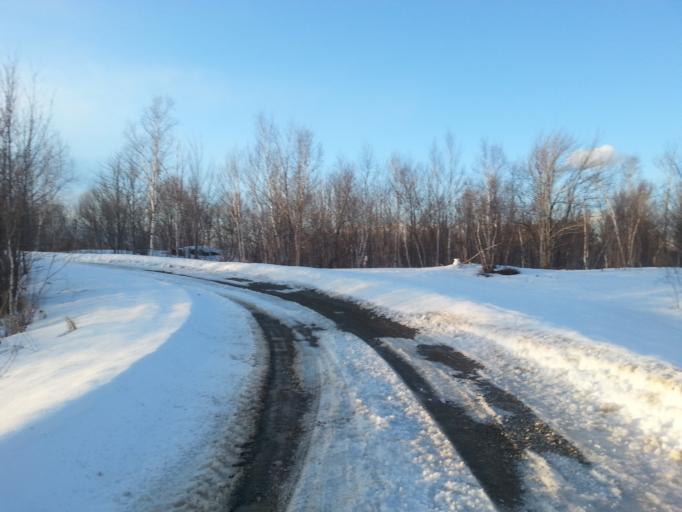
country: CA
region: Ontario
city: Greater Sudbury
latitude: 46.5902
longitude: -80.9860
